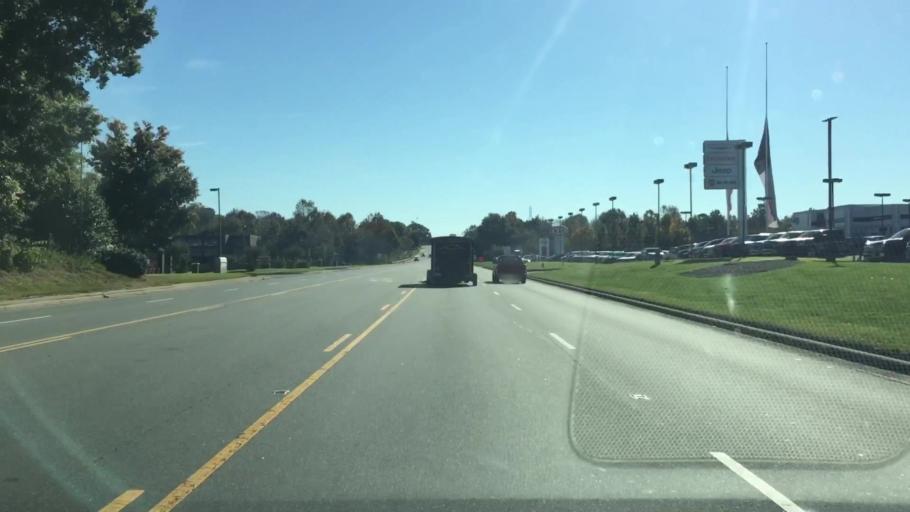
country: US
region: North Carolina
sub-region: Rowan County
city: Salisbury
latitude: 35.6463
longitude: -80.4903
